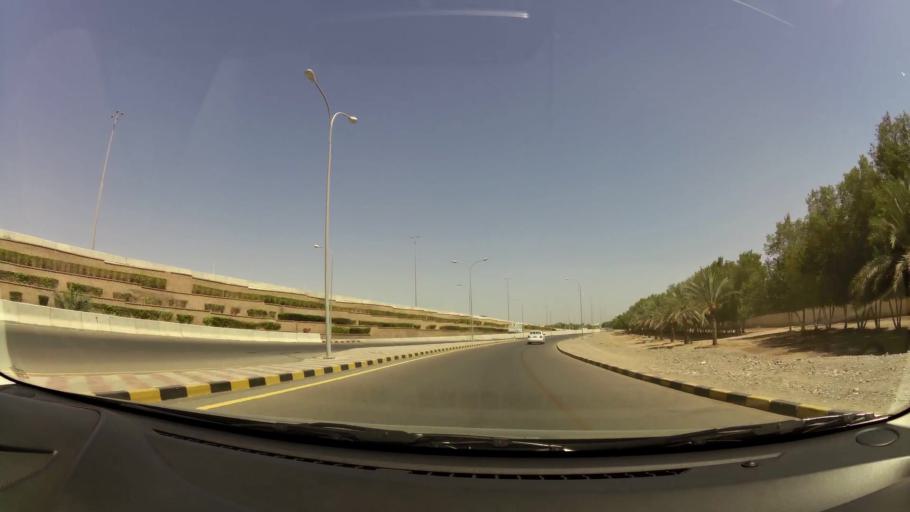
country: OM
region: Muhafazat Masqat
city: As Sib al Jadidah
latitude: 23.6140
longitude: 58.2453
